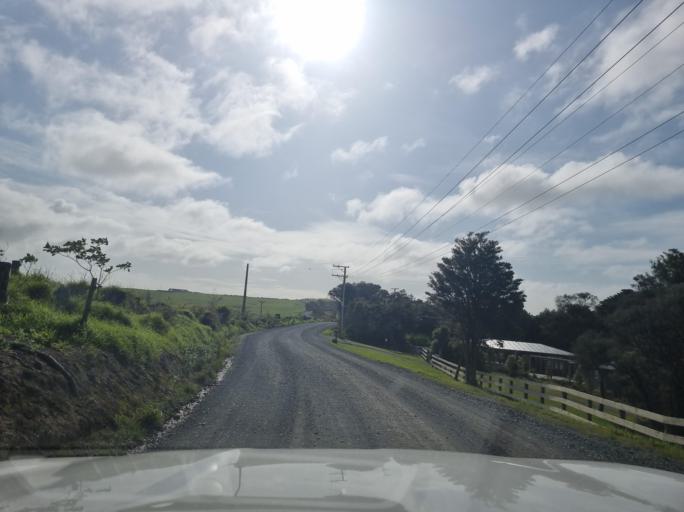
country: NZ
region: Northland
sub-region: Whangarei
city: Ruakaka
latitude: -36.0130
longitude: 174.4686
